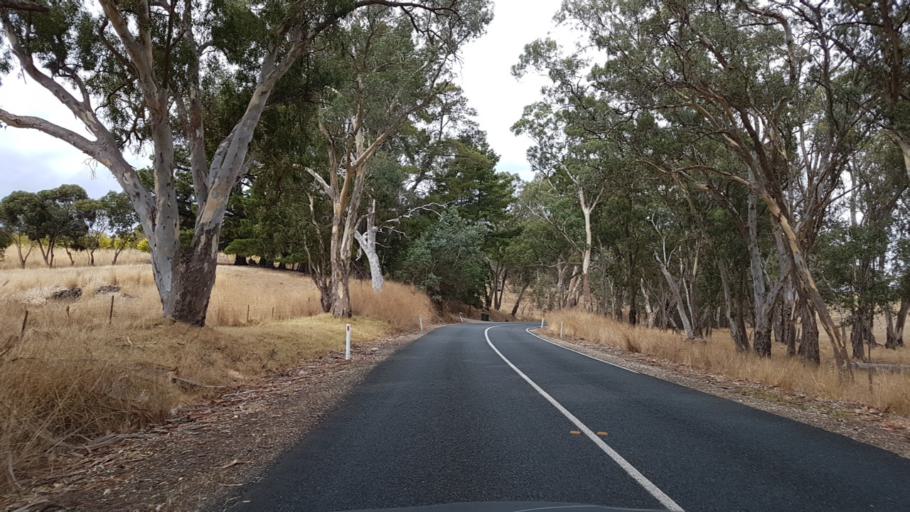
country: AU
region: South Australia
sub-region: Adelaide Hills
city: Birdwood
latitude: -34.7817
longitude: 138.9297
